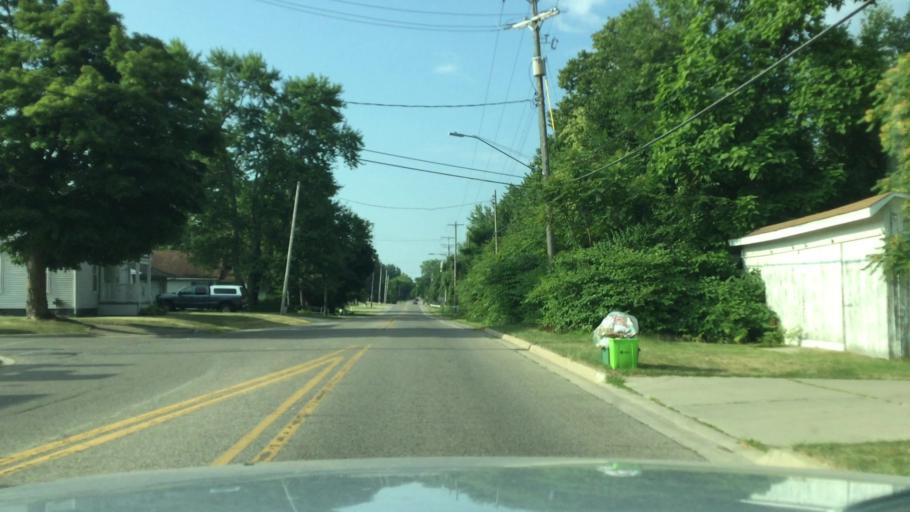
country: US
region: Michigan
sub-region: Genesee County
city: Flushing
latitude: 43.0622
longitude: -83.8625
